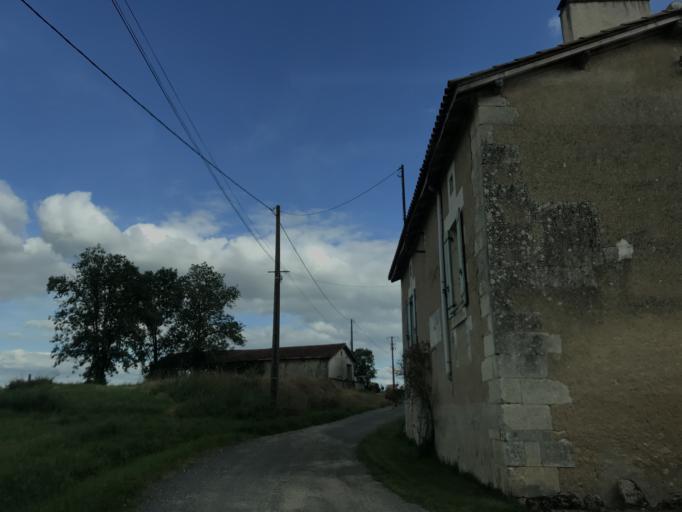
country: FR
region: Aquitaine
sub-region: Departement de la Dordogne
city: Saint-Aulaye
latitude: 45.2599
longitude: 0.1311
